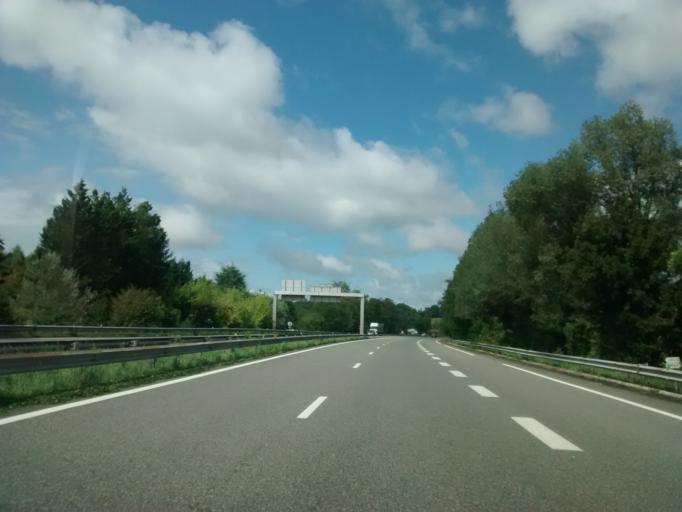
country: FR
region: Aquitaine
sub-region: Departement des Pyrenees-Atlantiques
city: Orthez
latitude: 43.4698
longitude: -0.7496
